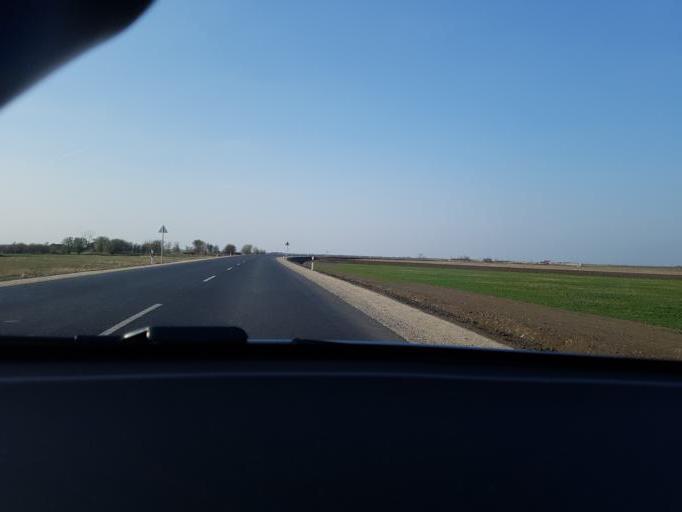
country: RO
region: Arad
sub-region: Comuna Nadlac
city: Nadlac
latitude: 46.1906
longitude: 20.7146
